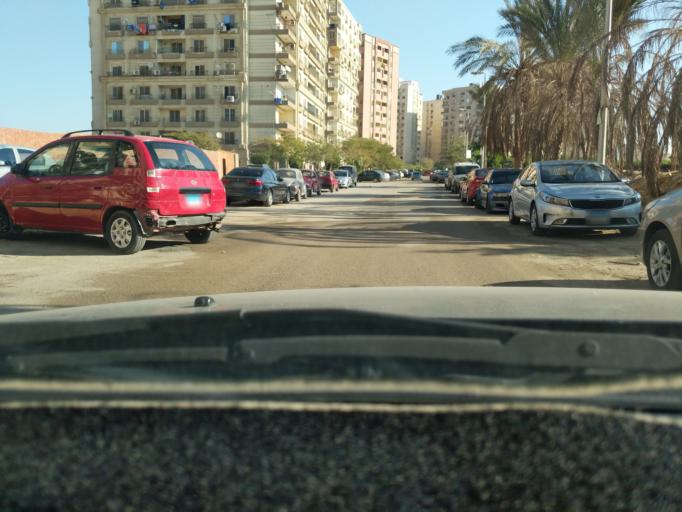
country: EG
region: Al Jizah
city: Al Hawamidiyah
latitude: 29.9635
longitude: 31.3203
